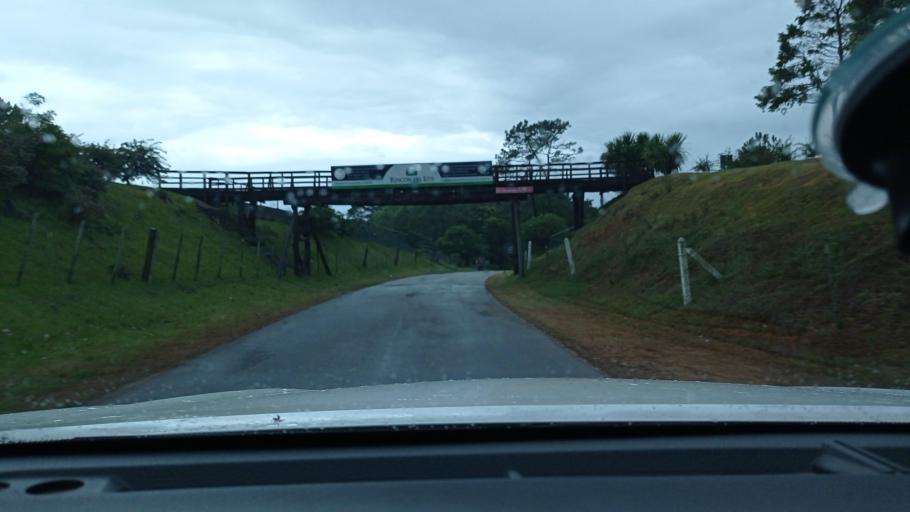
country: UY
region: Maldonado
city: Maldonado
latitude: -34.9245
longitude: -54.9112
